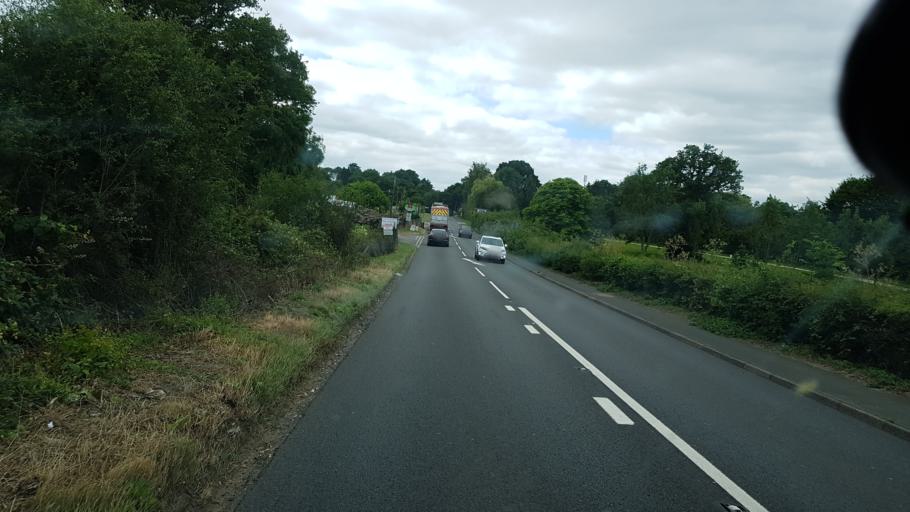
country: GB
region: England
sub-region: Surrey
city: Godstone
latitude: 51.2158
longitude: -0.0511
